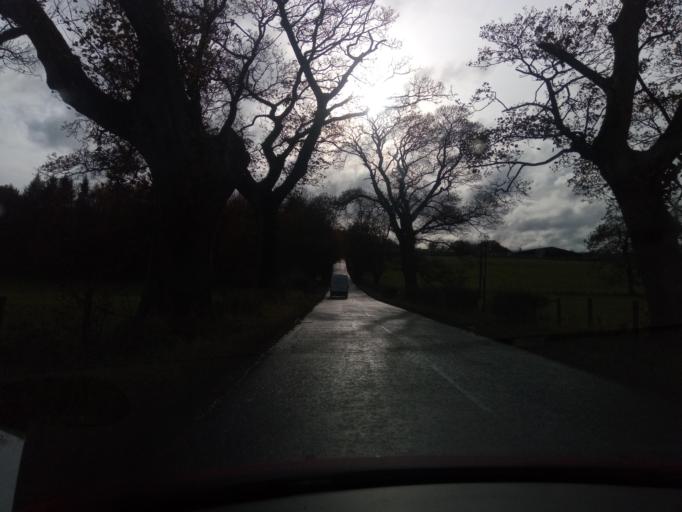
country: GB
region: England
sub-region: Northumberland
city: Birtley
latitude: 55.0653
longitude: -2.1920
